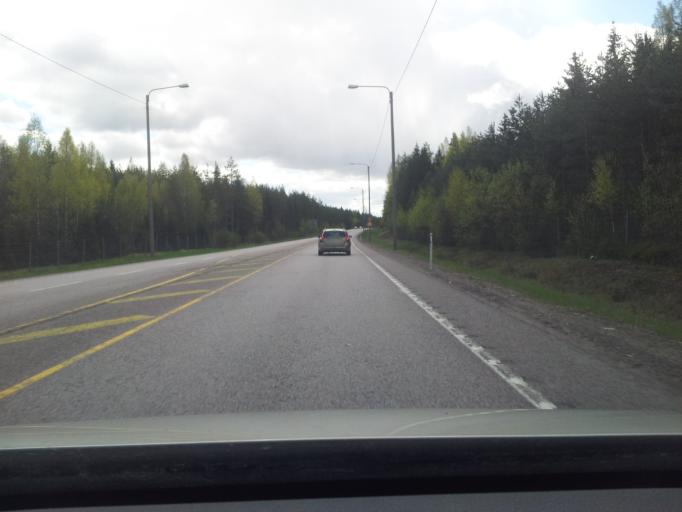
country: FI
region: Uusimaa
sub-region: Loviisa
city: Perna
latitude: 60.5136
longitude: 25.9646
